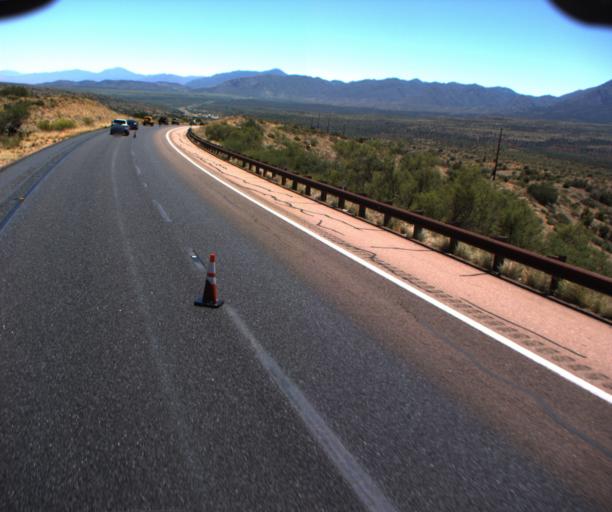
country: US
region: Arizona
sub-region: Gila County
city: Payson
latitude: 34.1467
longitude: -111.3503
